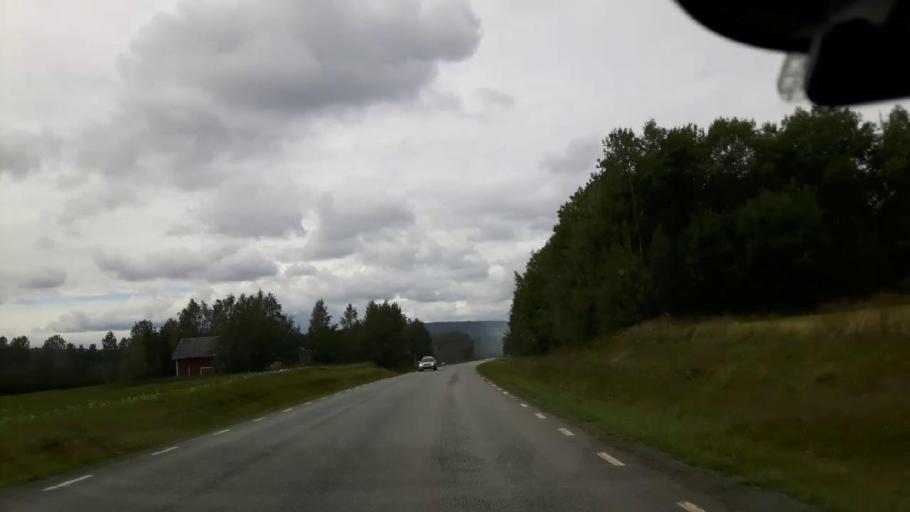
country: SE
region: Jaemtland
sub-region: Krokoms Kommun
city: Krokom
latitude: 63.4537
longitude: 14.1350
